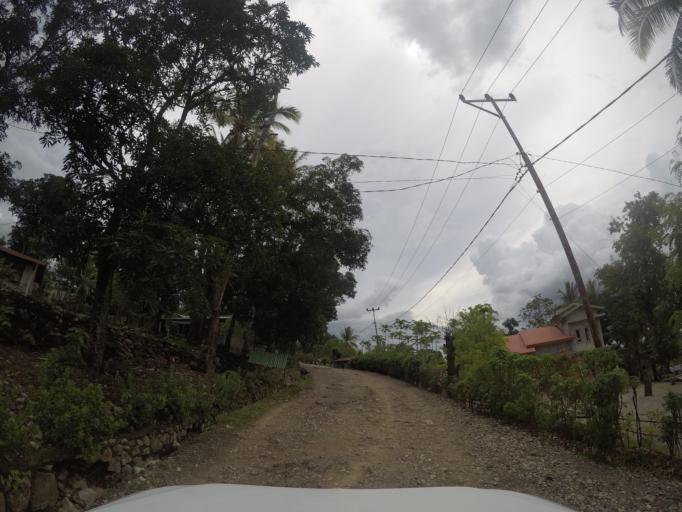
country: TL
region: Bobonaro
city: Maliana
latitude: -8.9934
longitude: 125.2184
